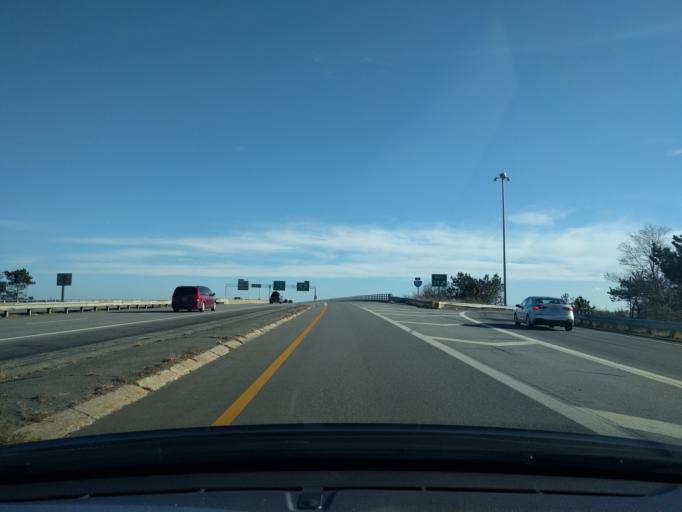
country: US
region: Maine
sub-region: Penobscot County
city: Bangor
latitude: 44.7851
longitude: -68.7788
